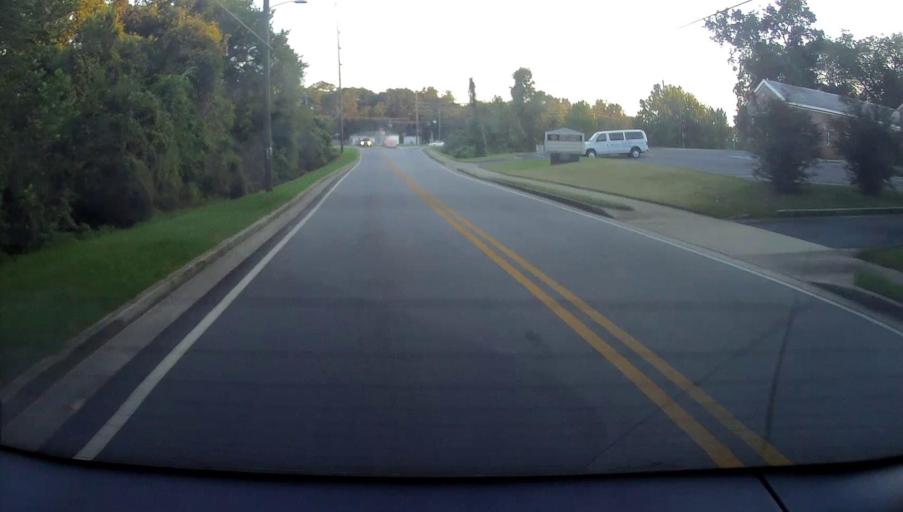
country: US
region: Georgia
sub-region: Houston County
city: Perry
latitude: 32.4578
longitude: -83.7384
